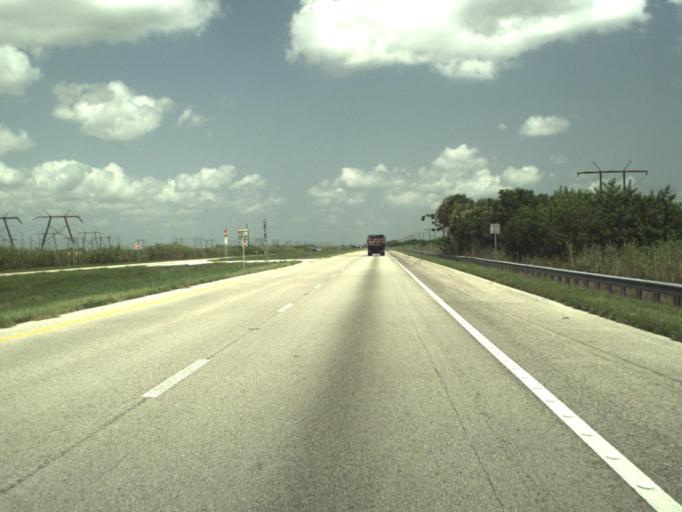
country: US
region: Florida
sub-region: Broward County
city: Weston
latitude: 26.2919
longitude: -80.5044
